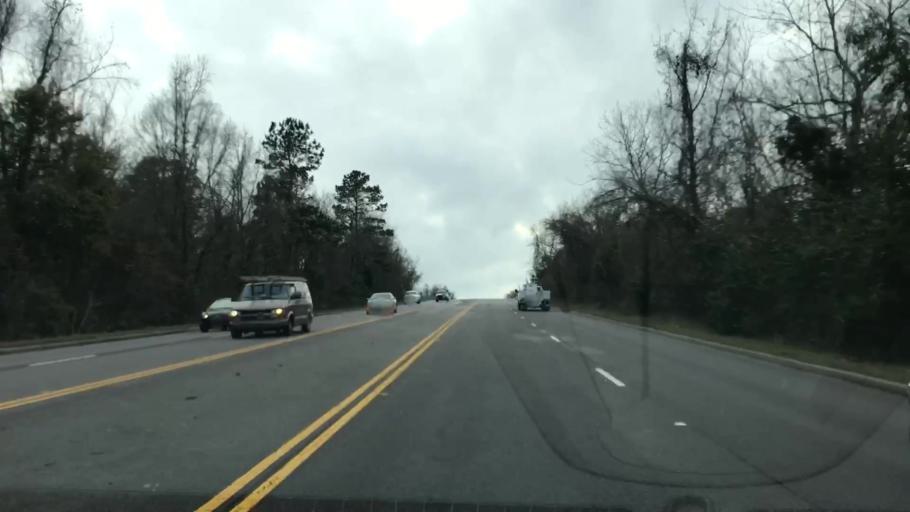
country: US
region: South Carolina
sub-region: Berkeley County
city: Moncks Corner
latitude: 33.2166
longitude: -79.9728
